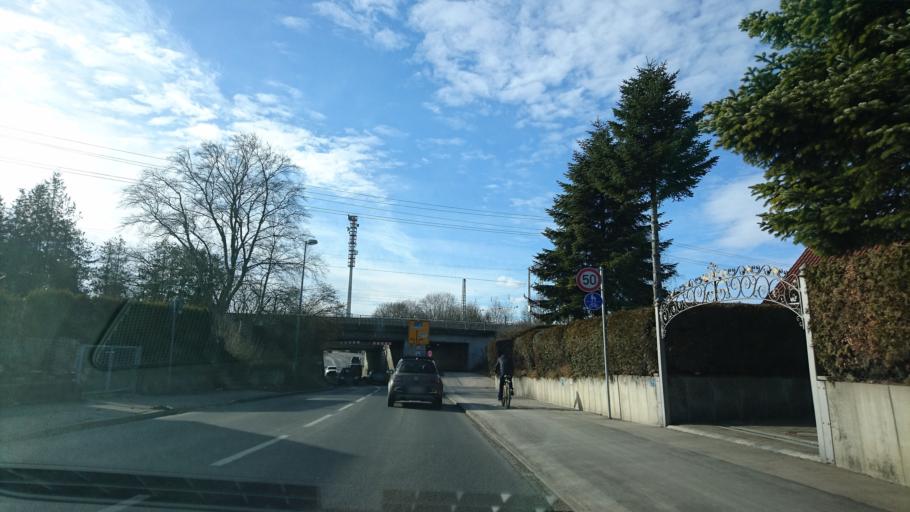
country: DE
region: Bavaria
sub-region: Swabia
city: Augsburg
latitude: 48.3895
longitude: 10.8709
